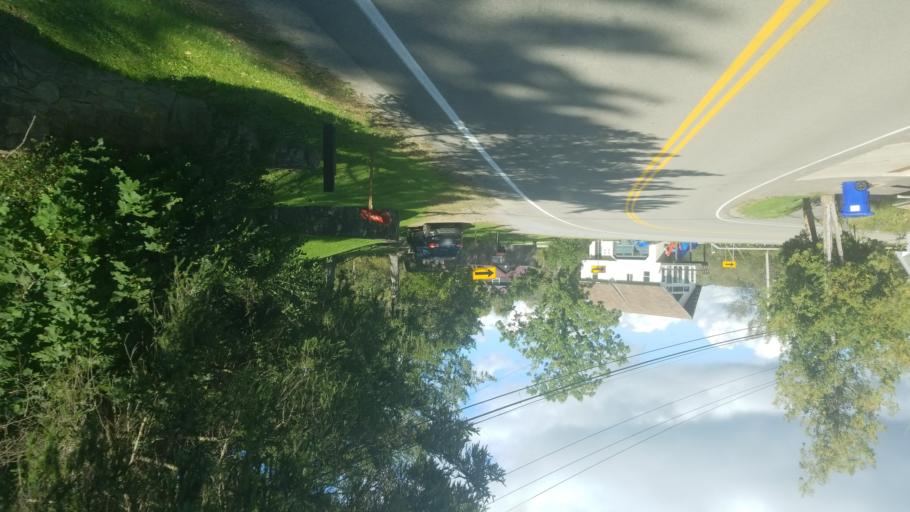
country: US
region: New York
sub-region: Allegany County
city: Cuba
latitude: 42.2586
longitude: -78.2925
